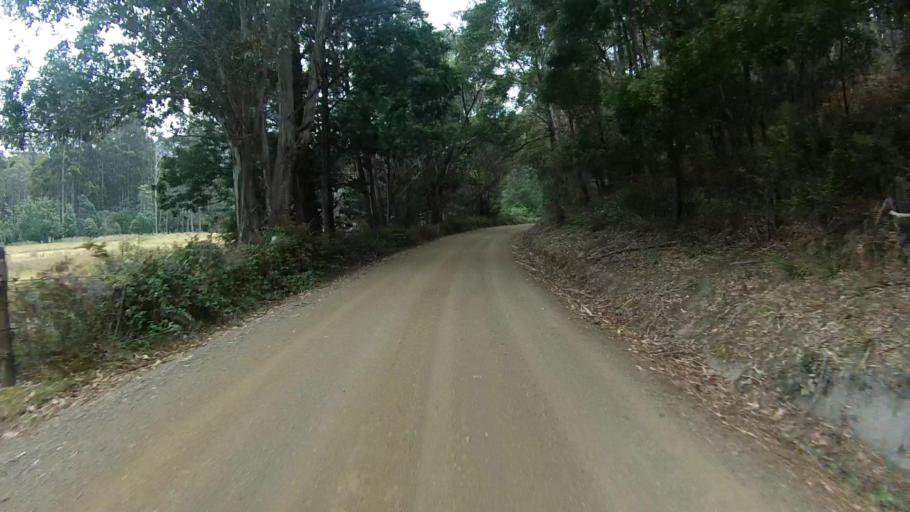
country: AU
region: Tasmania
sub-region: Huon Valley
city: Cygnet
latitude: -43.2315
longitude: 147.1589
